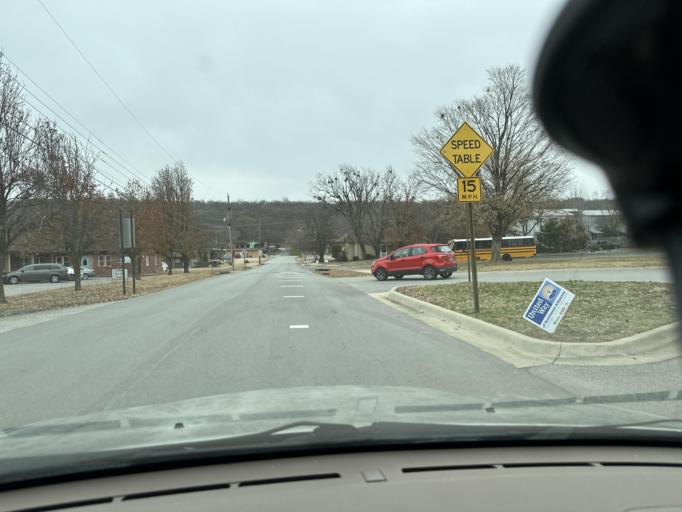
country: US
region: Arkansas
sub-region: Washington County
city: Fayetteville
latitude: 36.0886
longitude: -94.1570
